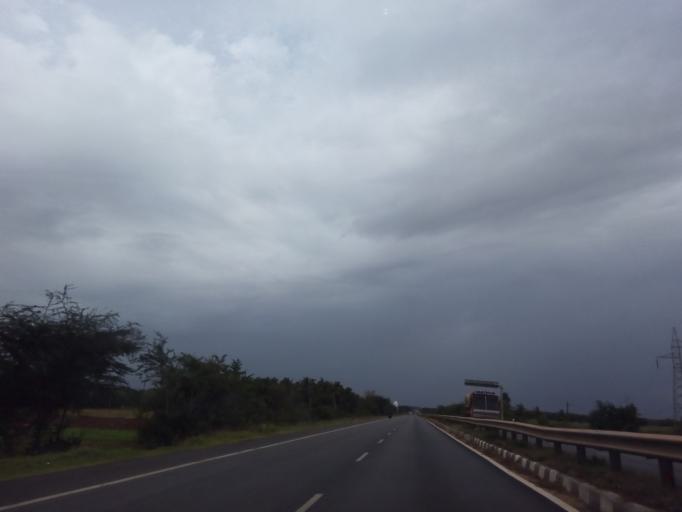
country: IN
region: Karnataka
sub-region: Davanagere
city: Harihar
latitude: 14.4772
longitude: 75.8184
